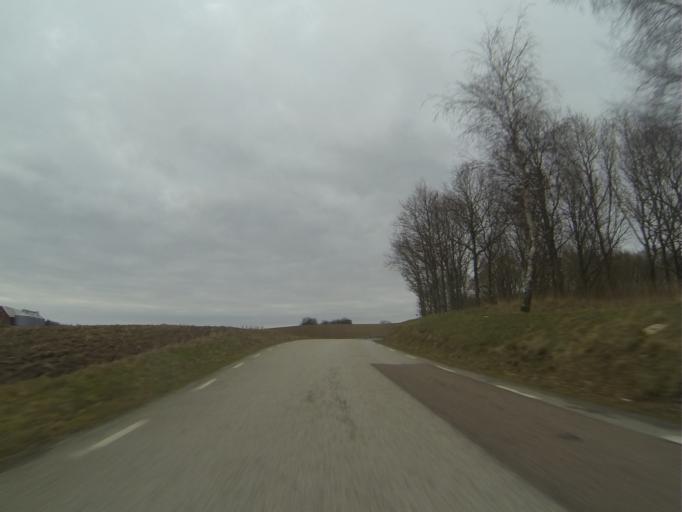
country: SE
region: Skane
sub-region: Skurups Kommun
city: Skurup
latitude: 55.5333
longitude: 13.4403
